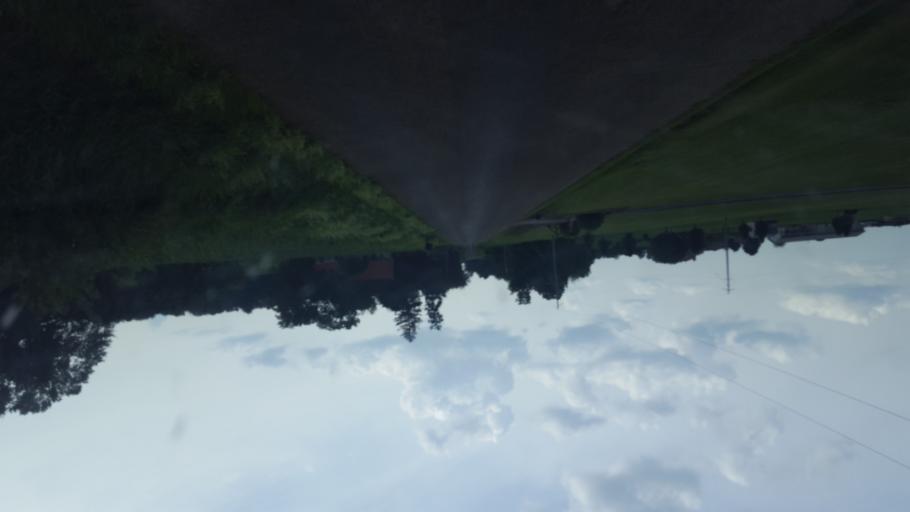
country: US
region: Ohio
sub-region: Knox County
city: Gambier
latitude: 40.3430
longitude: -82.3486
